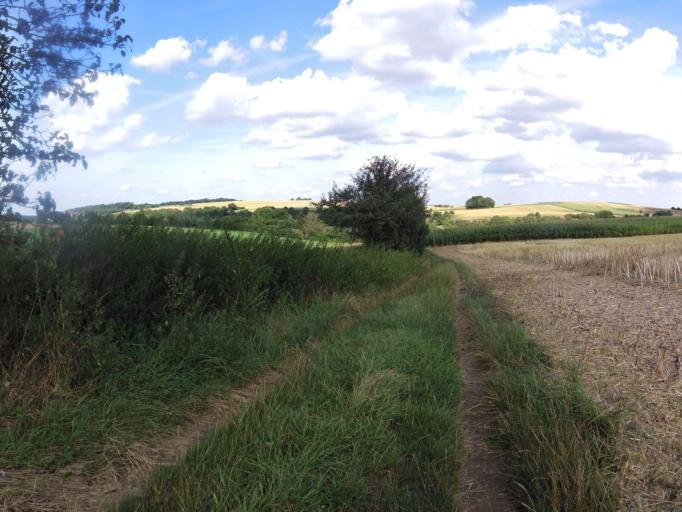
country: DE
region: Bavaria
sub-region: Regierungsbezirk Unterfranken
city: Reichenberg
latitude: 49.7209
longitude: 9.9118
